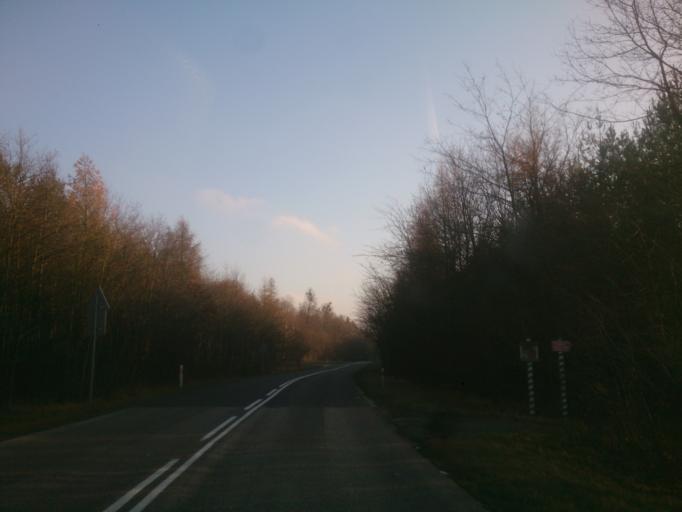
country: PL
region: Kujawsko-Pomorskie
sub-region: Powiat brodnicki
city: Brodnica
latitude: 53.2782
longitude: 19.4426
